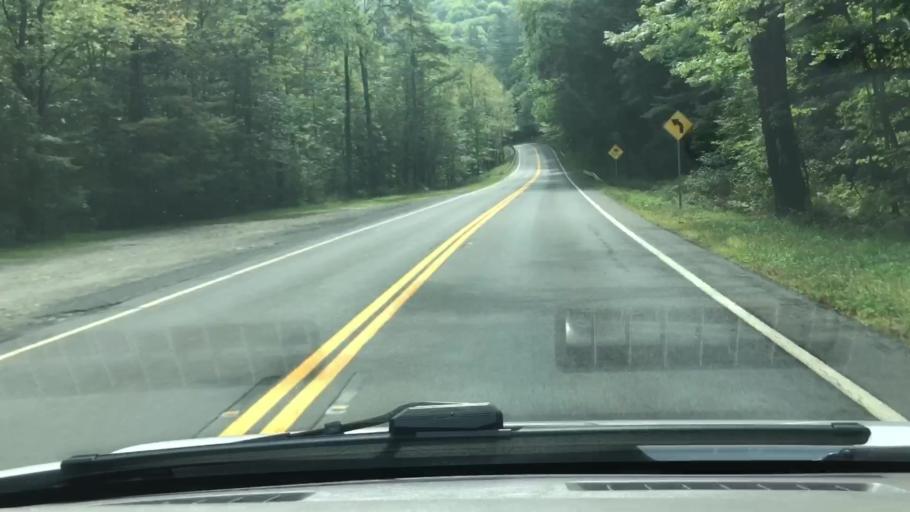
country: US
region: Massachusetts
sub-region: Franklin County
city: Charlemont
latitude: 42.6354
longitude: -72.9345
